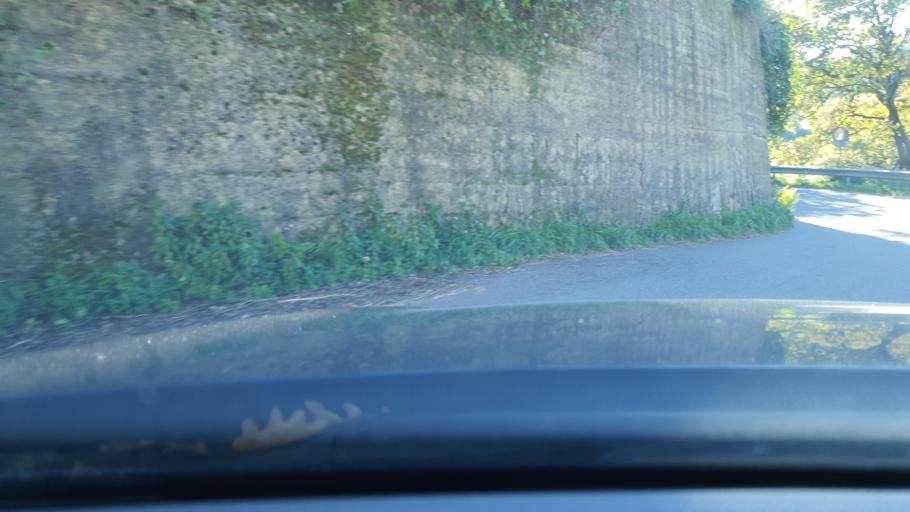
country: IT
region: Calabria
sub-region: Provincia di Catanzaro
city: Sant'Elia
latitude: 38.9577
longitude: 16.5799
